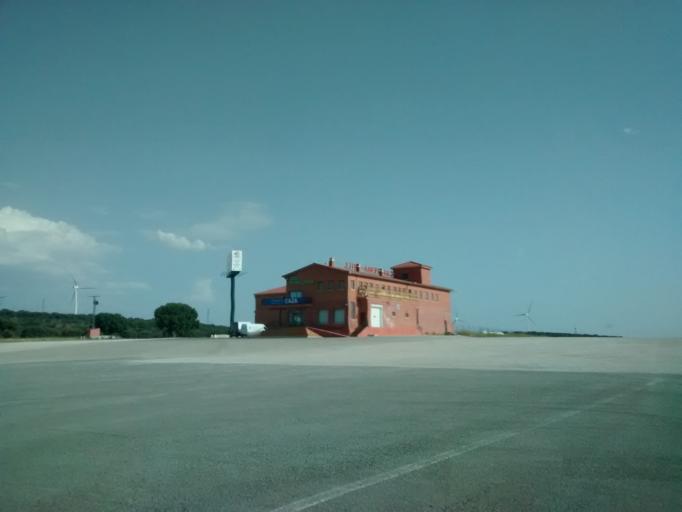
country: ES
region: Castille-La Mancha
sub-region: Provincia de Guadalajara
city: Sauca
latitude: 41.0259
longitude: -2.5204
